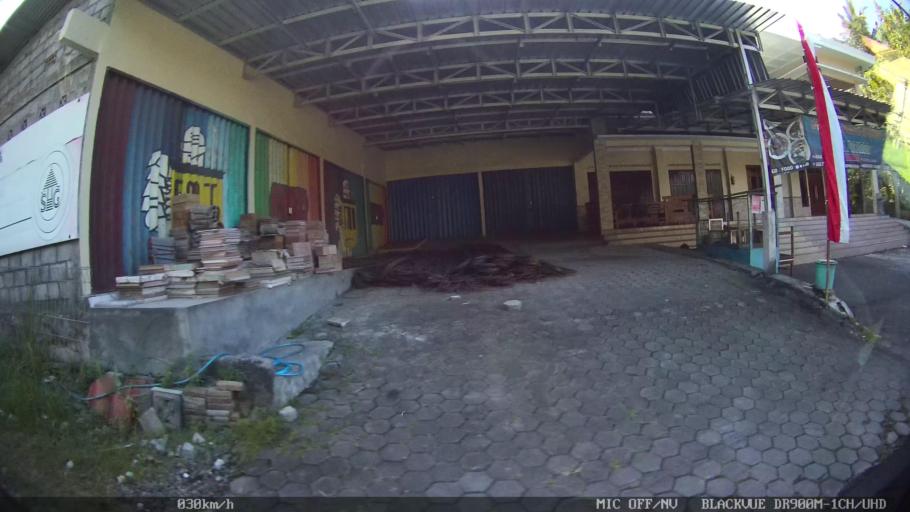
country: ID
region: Daerah Istimewa Yogyakarta
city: Kasihan
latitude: -7.8228
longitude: 110.2738
